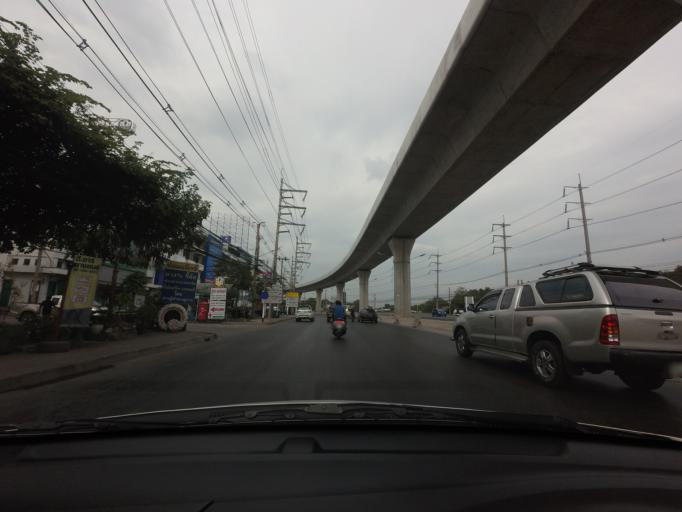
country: TH
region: Samut Prakan
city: Samut Prakan
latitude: 13.5886
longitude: 100.6094
